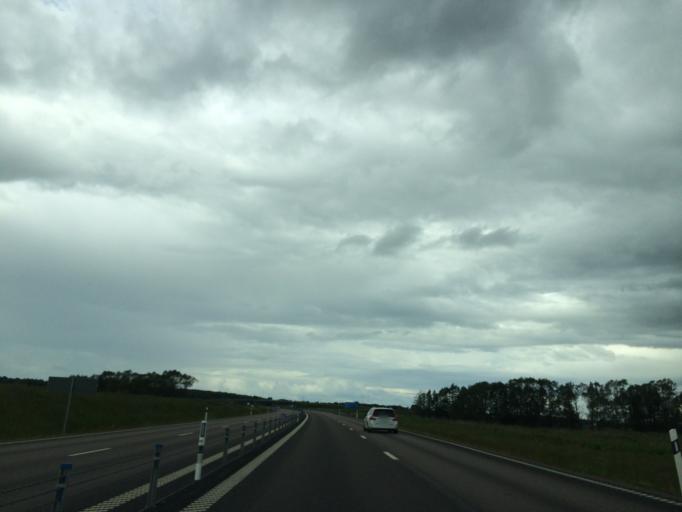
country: SE
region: OEstergoetland
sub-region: Mjolby Kommun
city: Mjolby
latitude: 58.3996
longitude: 15.0998
